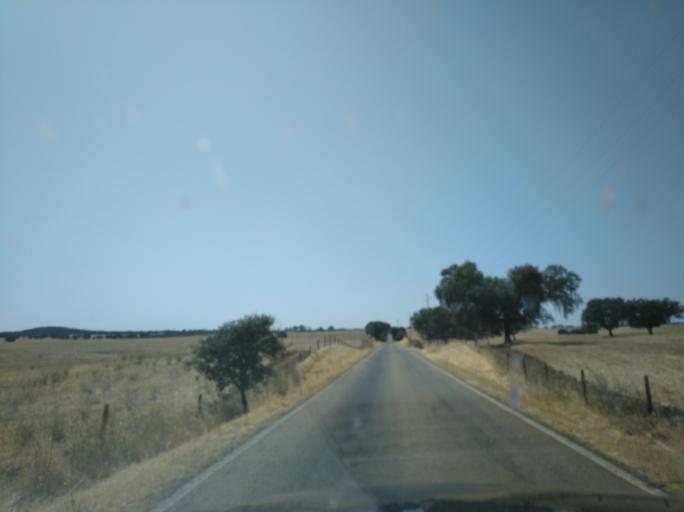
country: PT
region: Portalegre
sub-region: Campo Maior
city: Campo Maior
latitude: 39.0129
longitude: -6.9828
